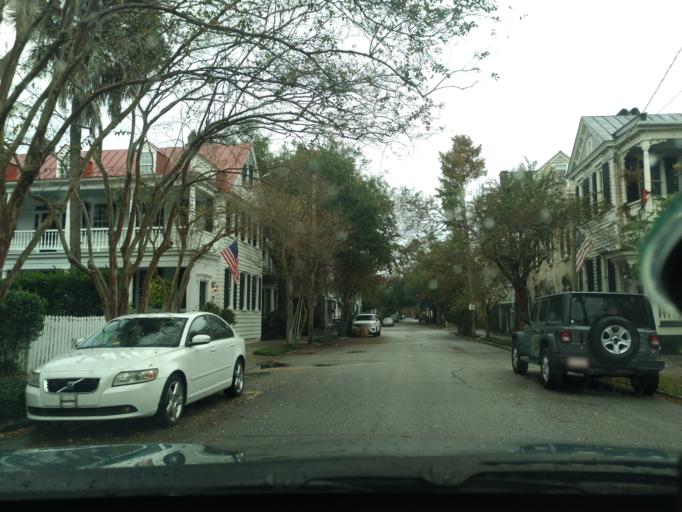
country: US
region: South Carolina
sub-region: Charleston County
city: Charleston
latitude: 32.7819
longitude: -79.9421
